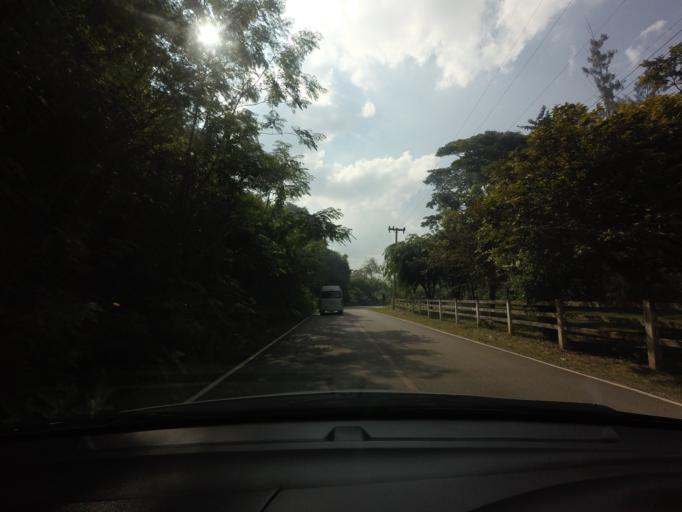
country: TH
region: Nakhon Ratchasima
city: Pak Chong
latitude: 14.5299
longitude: 101.3919
